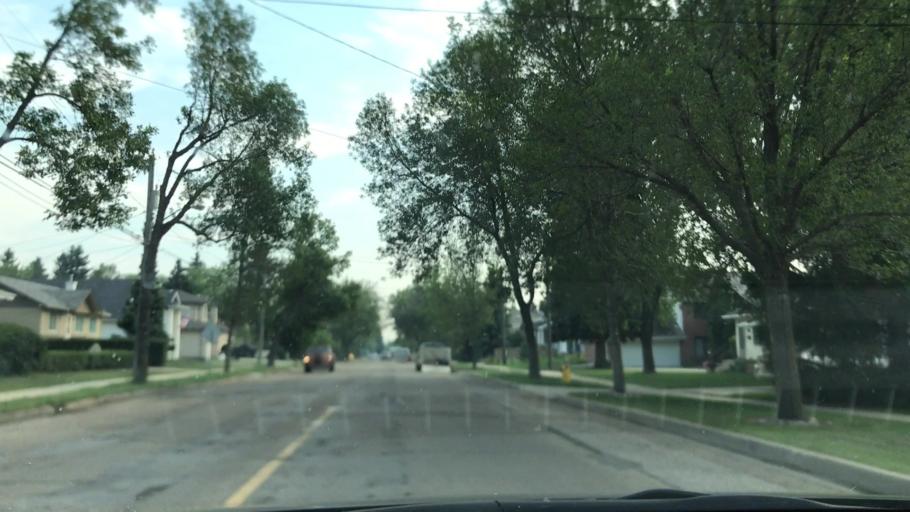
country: CA
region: Alberta
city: Edmonton
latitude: 53.4940
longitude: -113.5119
